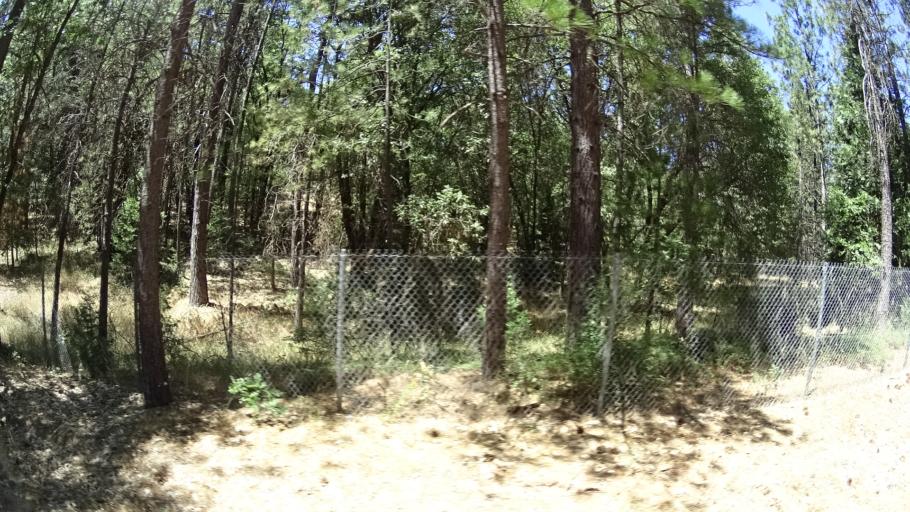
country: US
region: California
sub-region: Calaveras County
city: Mountain Ranch
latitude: 38.3202
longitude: -120.5229
